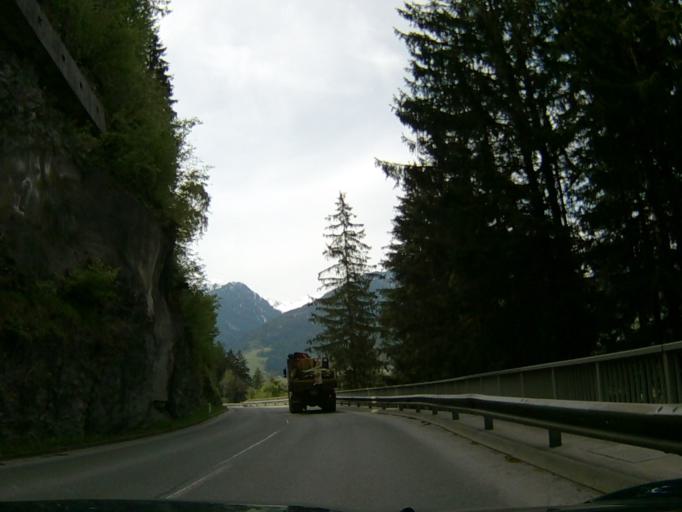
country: AT
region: Tyrol
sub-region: Politischer Bezirk Schwaz
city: Hainzenberg
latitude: 47.2234
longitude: 11.8903
